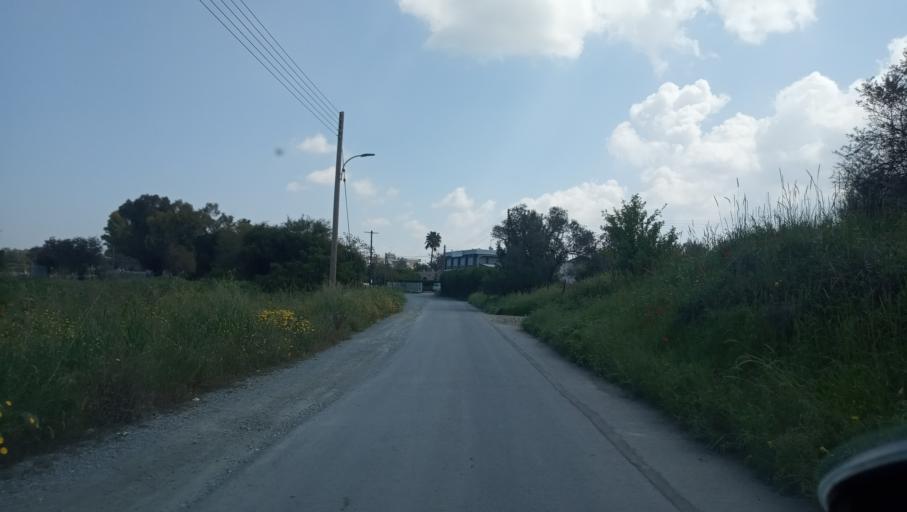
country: CY
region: Lefkosia
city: Dali
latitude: 35.0245
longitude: 33.4156
